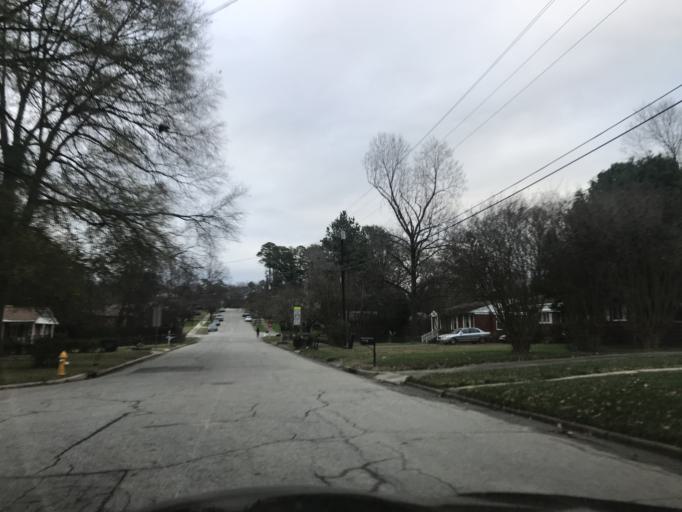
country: US
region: North Carolina
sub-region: Wake County
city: Raleigh
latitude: 35.7538
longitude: -78.6292
